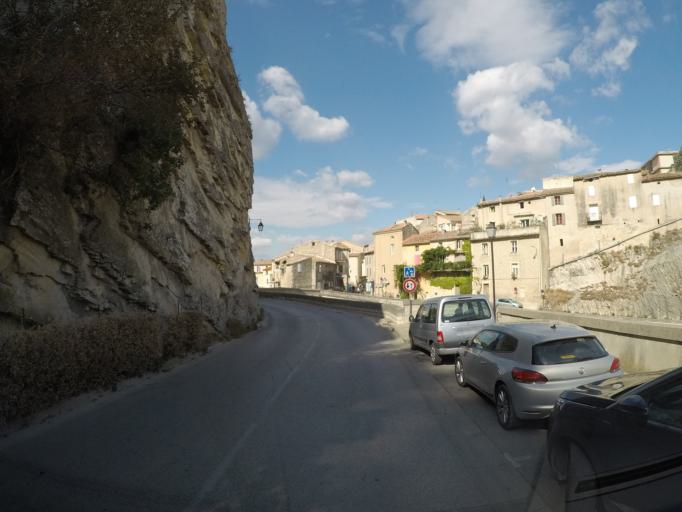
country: FR
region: Provence-Alpes-Cote d'Azur
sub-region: Departement du Vaucluse
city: Vaison-la-Romaine
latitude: 44.2383
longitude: 5.0751
